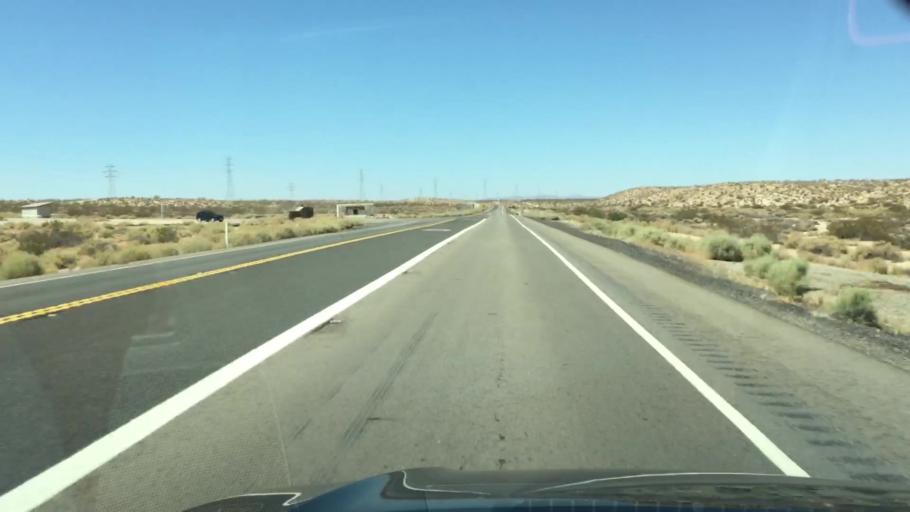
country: US
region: California
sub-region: Kern County
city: Boron
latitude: 35.0759
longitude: -117.5613
